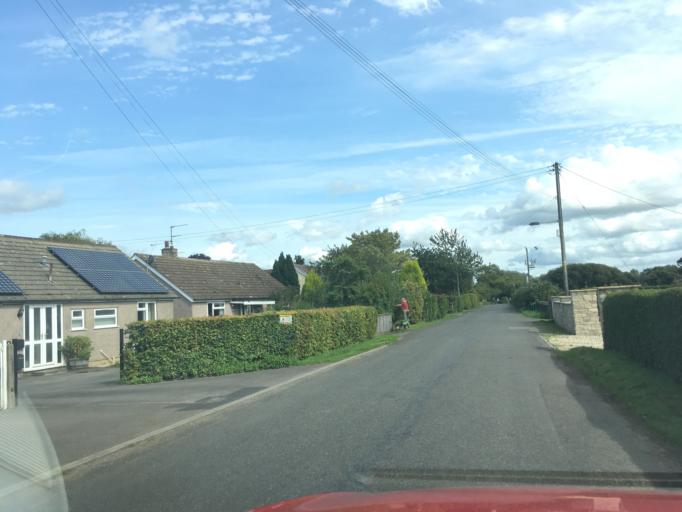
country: GB
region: England
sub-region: South Gloucestershire
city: Wickwar
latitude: 51.6000
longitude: -2.4392
